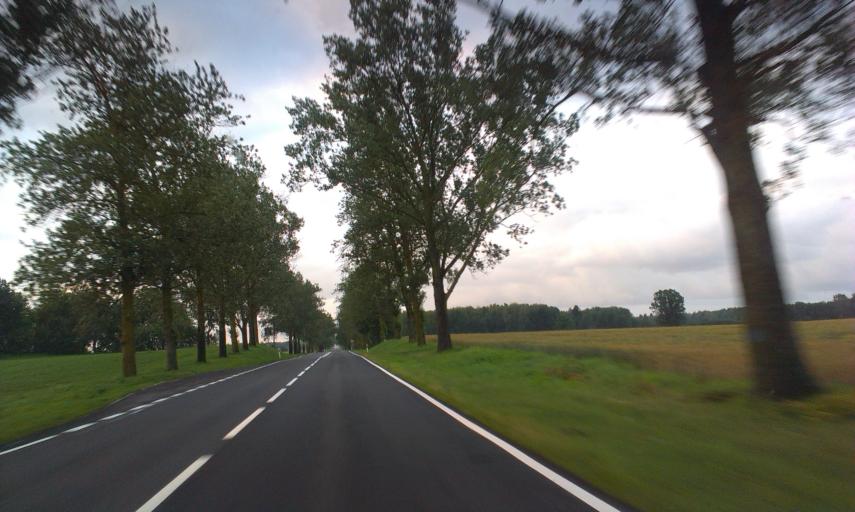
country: PL
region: Greater Poland Voivodeship
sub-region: Powiat zlotowski
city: Okonek
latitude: 53.5929
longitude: 16.8159
